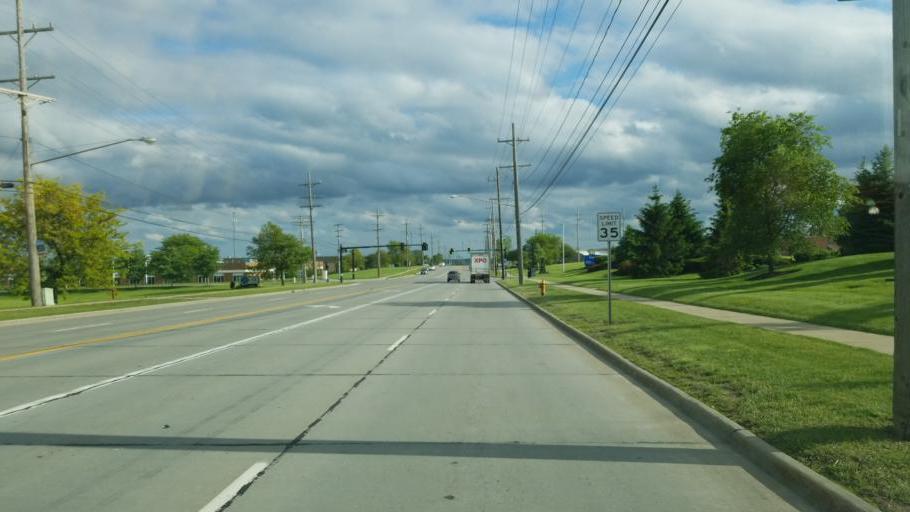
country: US
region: Ohio
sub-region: Cuyahoga County
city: Solon
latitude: 41.3824
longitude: -81.4693
